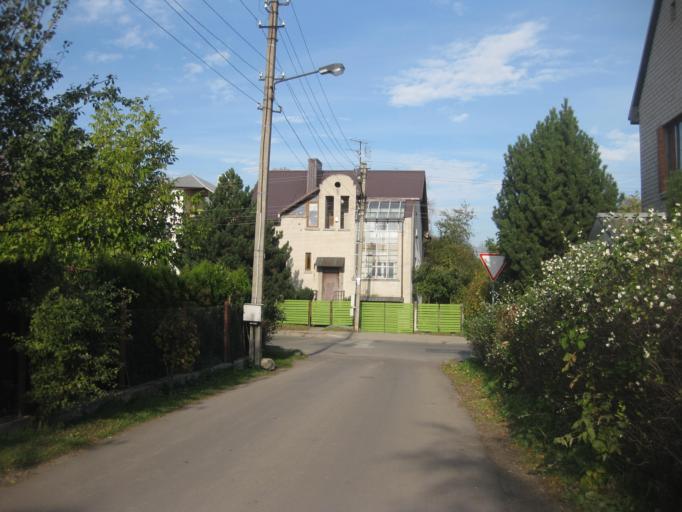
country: LT
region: Kauno apskritis
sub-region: Kaunas
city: Aleksotas
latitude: 54.8872
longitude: 23.8937
